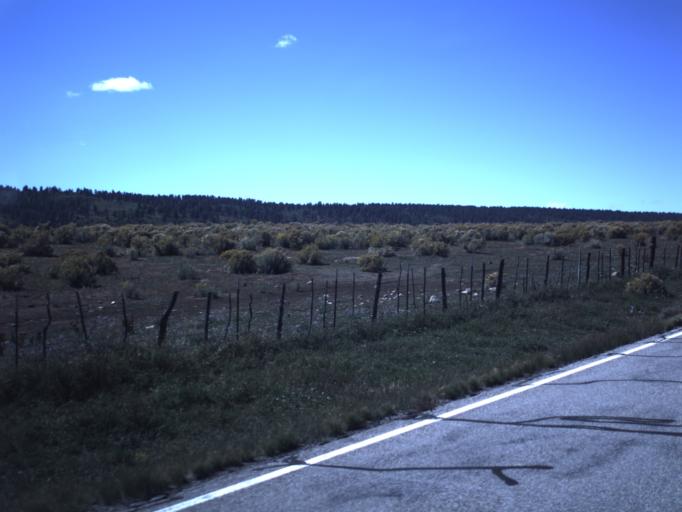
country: US
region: Utah
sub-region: Grand County
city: Moab
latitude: 38.3271
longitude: -109.1275
